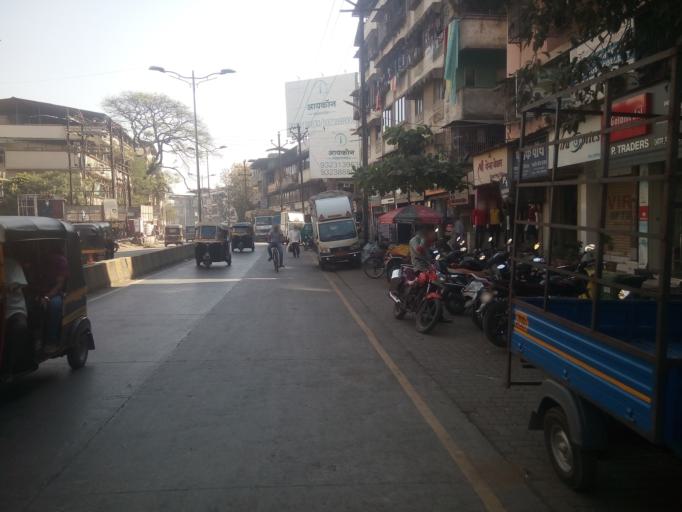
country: IN
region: Maharashtra
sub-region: Thane
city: Dombivli
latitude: 19.2137
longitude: 73.0914
